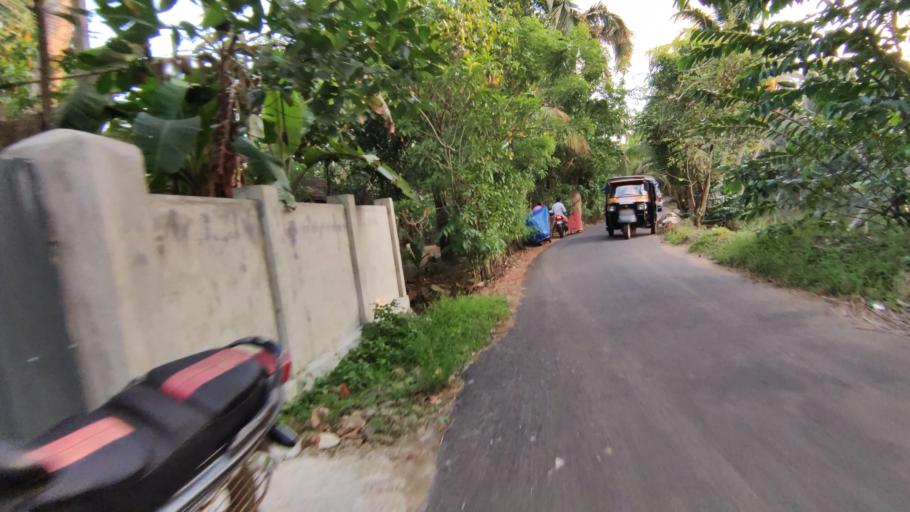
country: IN
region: Kerala
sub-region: Kottayam
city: Kottayam
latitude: 9.5796
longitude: 76.4473
